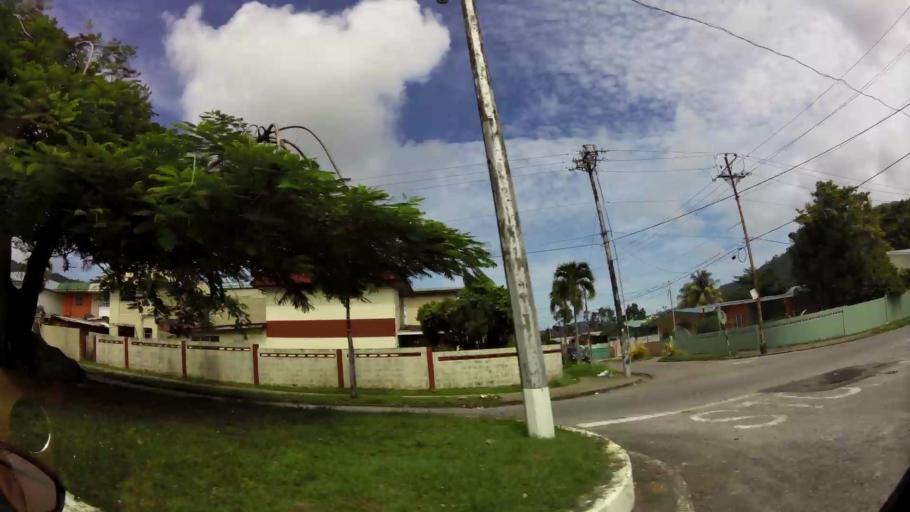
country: TT
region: Diego Martin
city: Petit Valley
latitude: 10.7181
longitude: -61.5606
